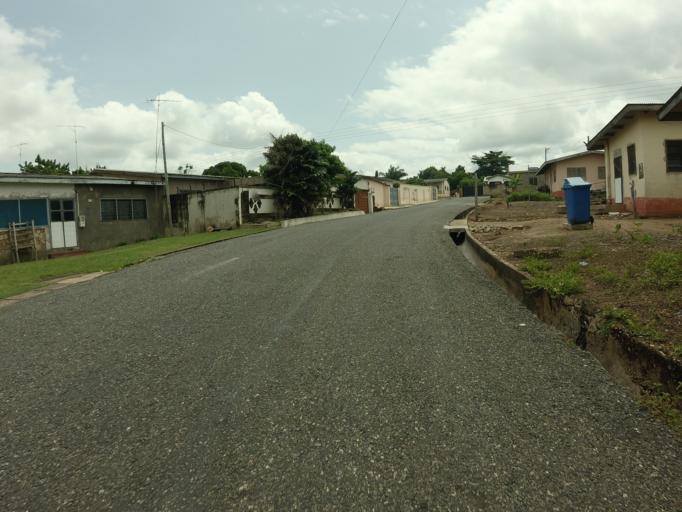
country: GH
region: Volta
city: Ho
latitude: 6.5916
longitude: 0.4750
